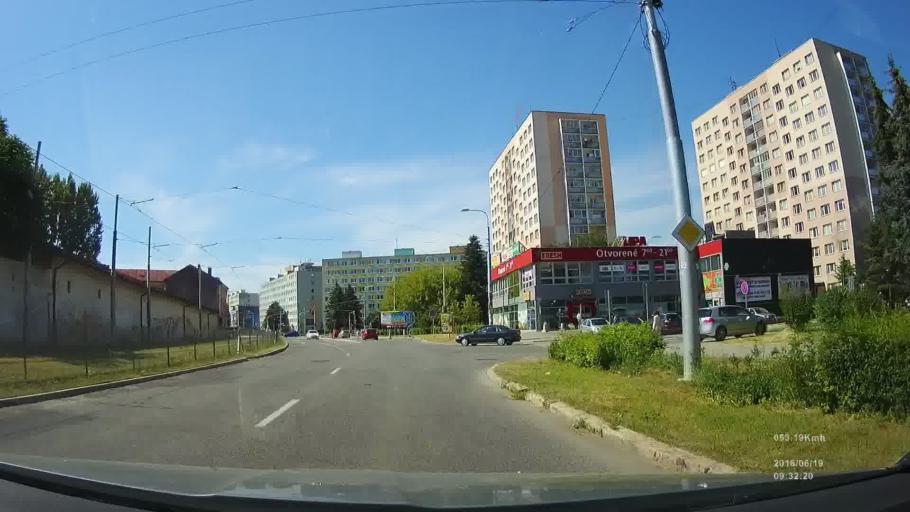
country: SK
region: Kosicky
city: Kosice
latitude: 48.7232
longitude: 21.2490
